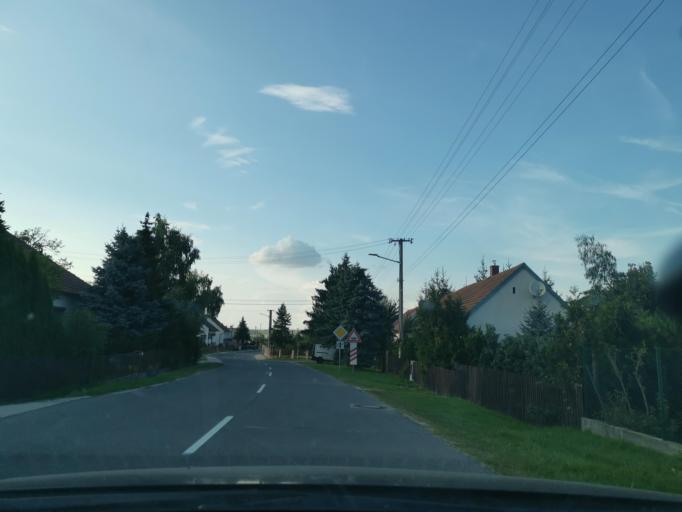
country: SK
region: Trnavsky
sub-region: Okres Senica
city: Senica
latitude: 48.6578
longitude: 17.2653
